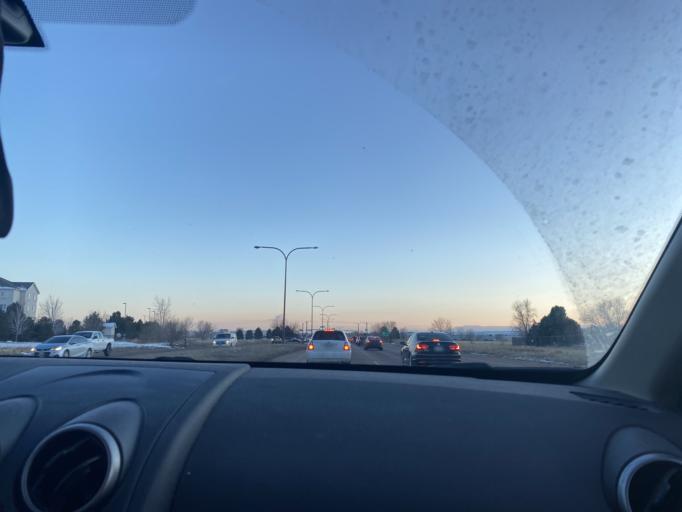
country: US
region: Colorado
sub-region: El Paso County
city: Cimarron Hills
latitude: 38.8097
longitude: -104.7301
